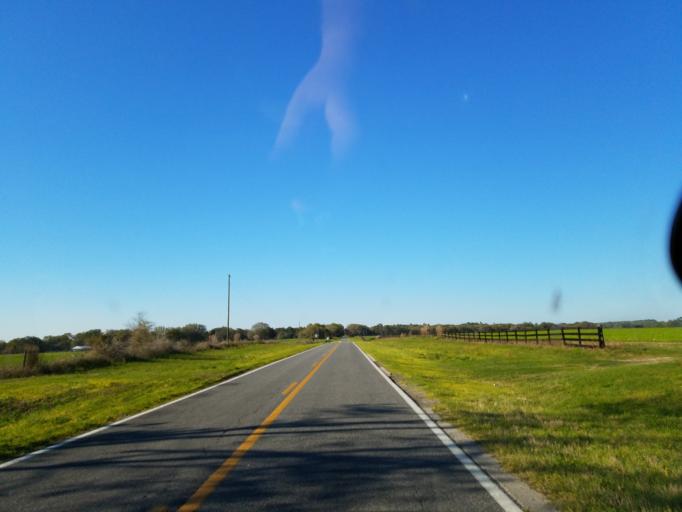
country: US
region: Florida
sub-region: Suwannee County
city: Wellborn
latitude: 30.1347
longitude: -82.8871
